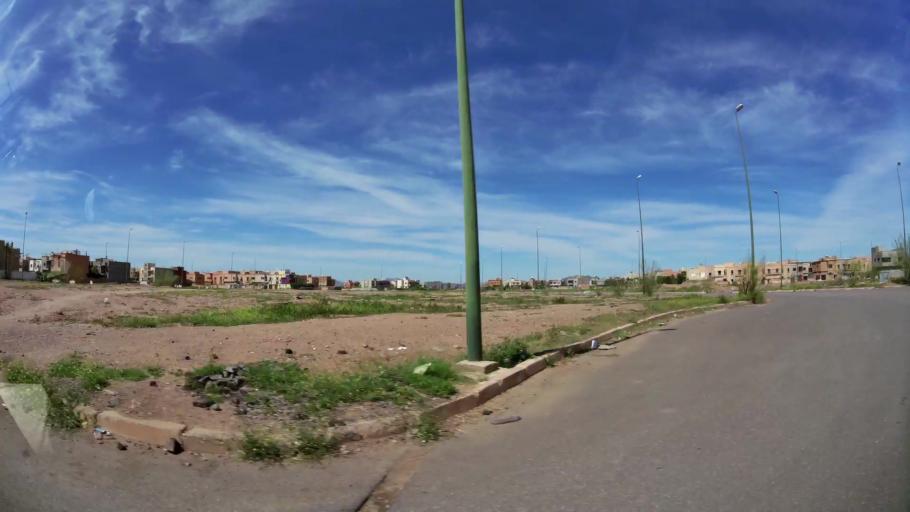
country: MA
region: Marrakech-Tensift-Al Haouz
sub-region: Marrakech
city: Marrakesh
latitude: 31.6496
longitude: -8.0756
